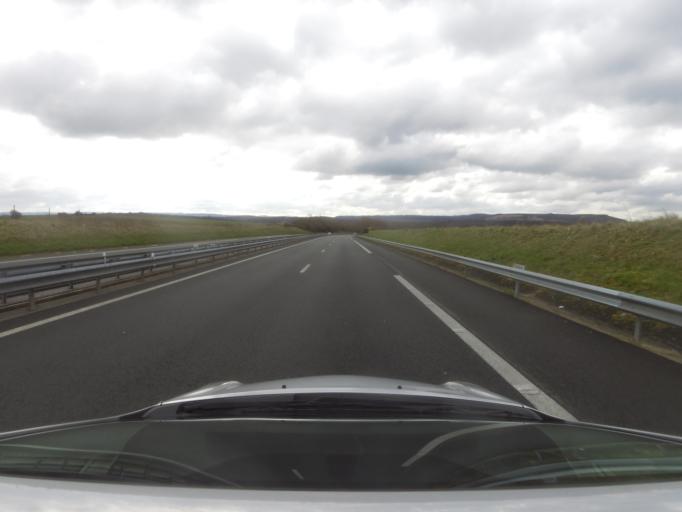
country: FR
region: Nord-Pas-de-Calais
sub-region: Departement du Pas-de-Calais
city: Isques
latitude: 50.6551
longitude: 1.6584
